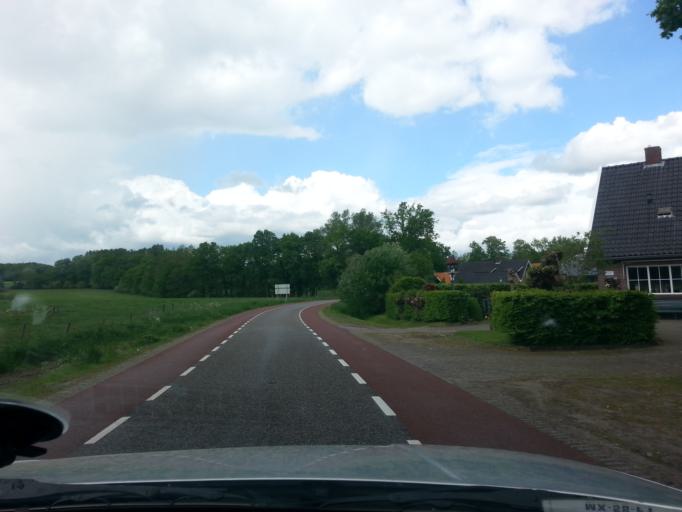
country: NL
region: Overijssel
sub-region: Gemeente Losser
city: Losser
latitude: 52.3167
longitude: 6.9966
